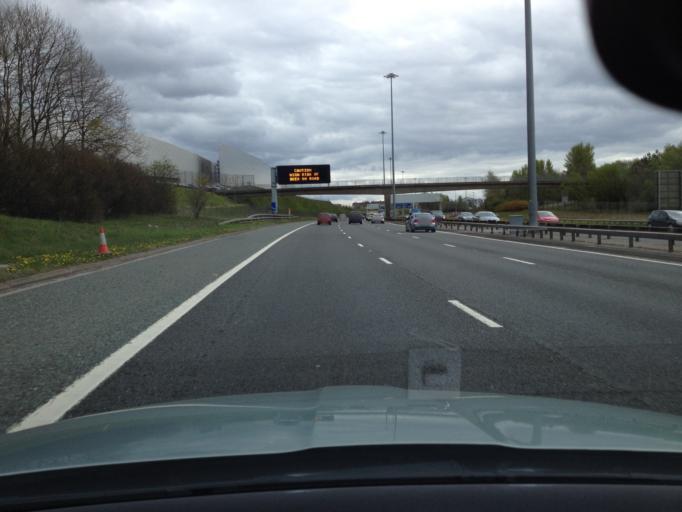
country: GB
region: Scotland
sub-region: North Lanarkshire
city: Stepps
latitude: 55.8697
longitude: -4.1417
